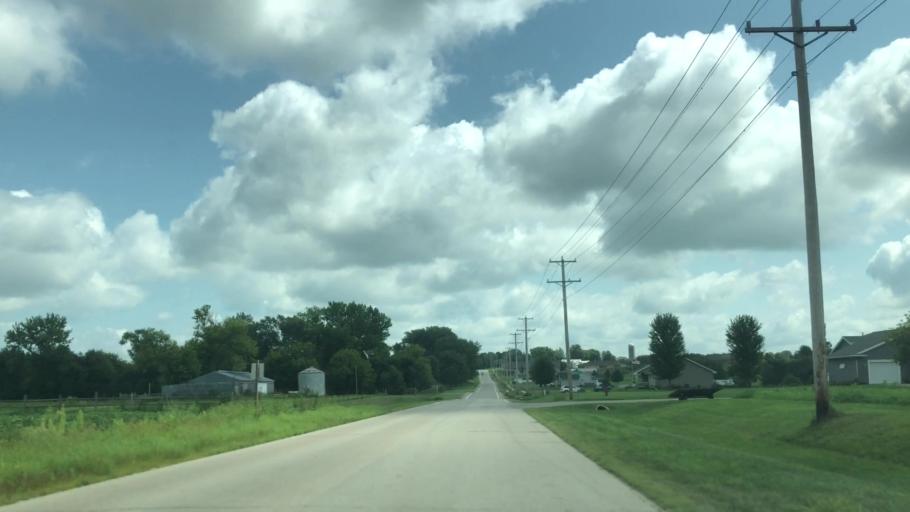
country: US
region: Iowa
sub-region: Marshall County
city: Marshalltown
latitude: 42.0178
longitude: -92.9562
